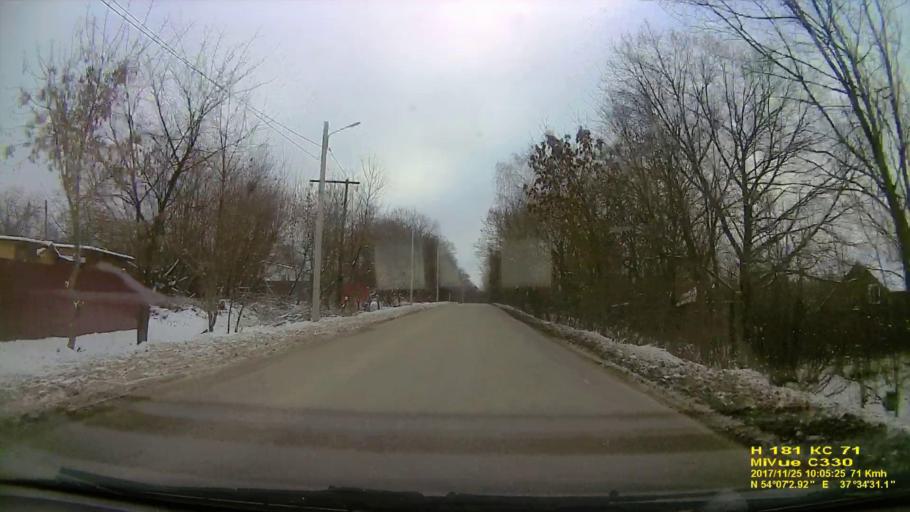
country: RU
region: Tula
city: Mendeleyevskiy
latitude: 54.1174
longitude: 37.5757
